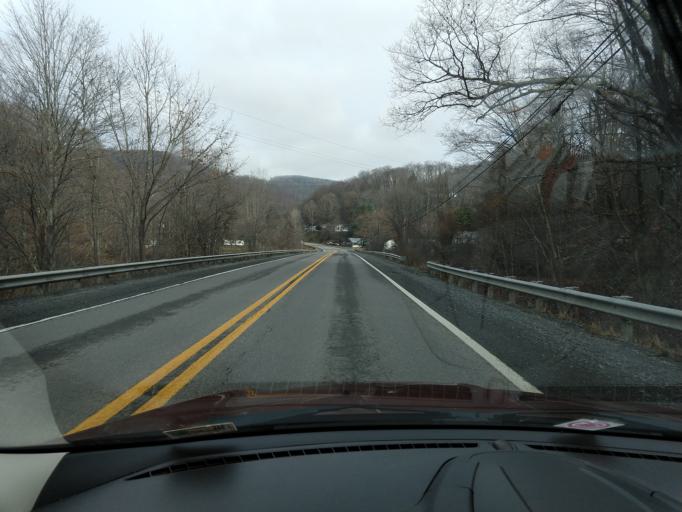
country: US
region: West Virginia
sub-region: Greenbrier County
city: Rainelle
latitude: 38.0465
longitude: -80.7224
